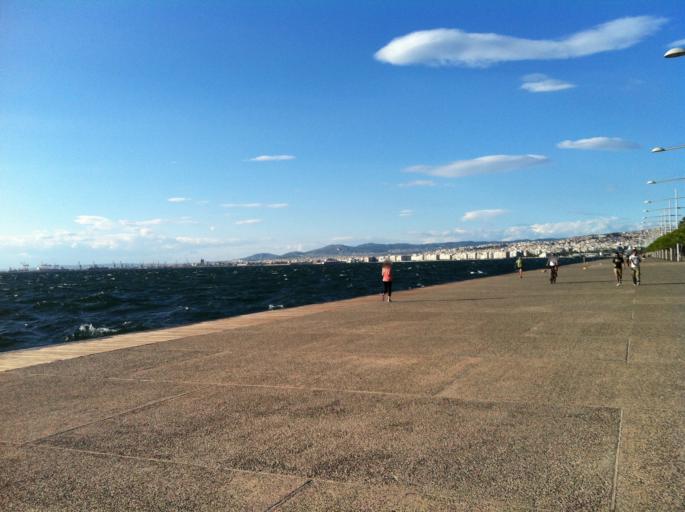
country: GR
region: Central Macedonia
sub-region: Nomos Thessalonikis
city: Kalamaria
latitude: 40.6002
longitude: 22.9491
